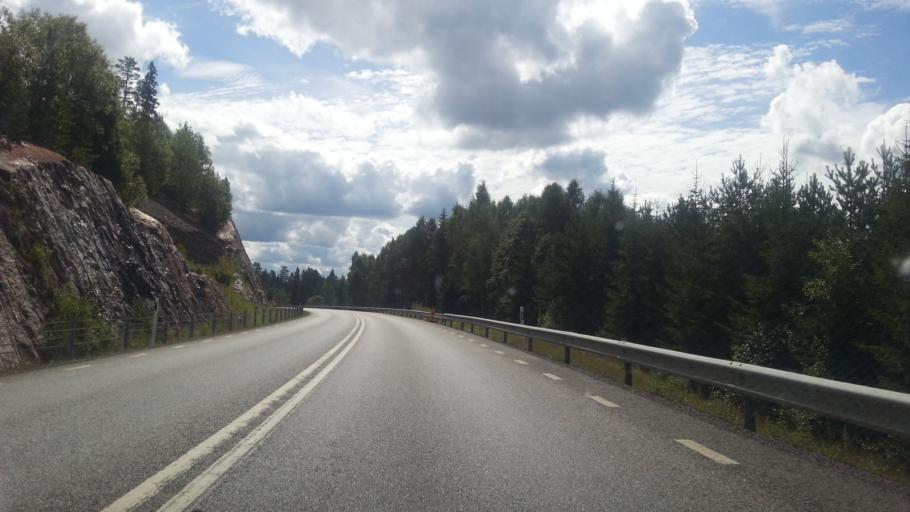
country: SE
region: OErebro
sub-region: Ljusnarsbergs Kommun
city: Kopparberg
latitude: 59.8534
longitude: 15.0609
